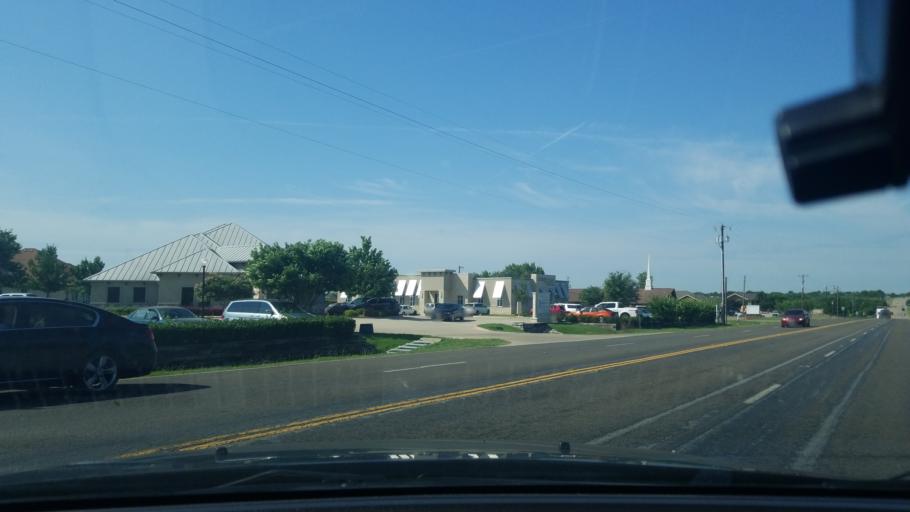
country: US
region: Texas
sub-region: Dallas County
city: Sunnyvale
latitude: 32.7746
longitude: -96.5708
